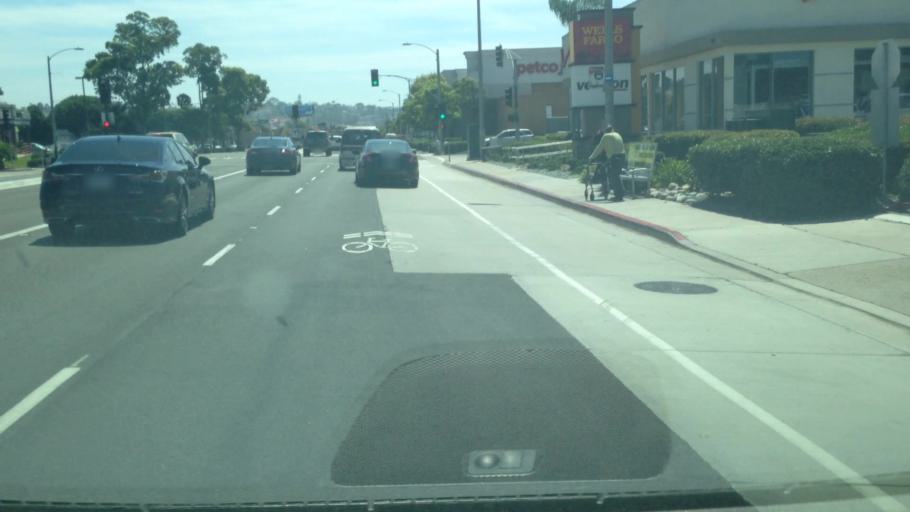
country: US
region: California
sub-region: San Diego County
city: San Diego
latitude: 32.7537
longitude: -117.2123
